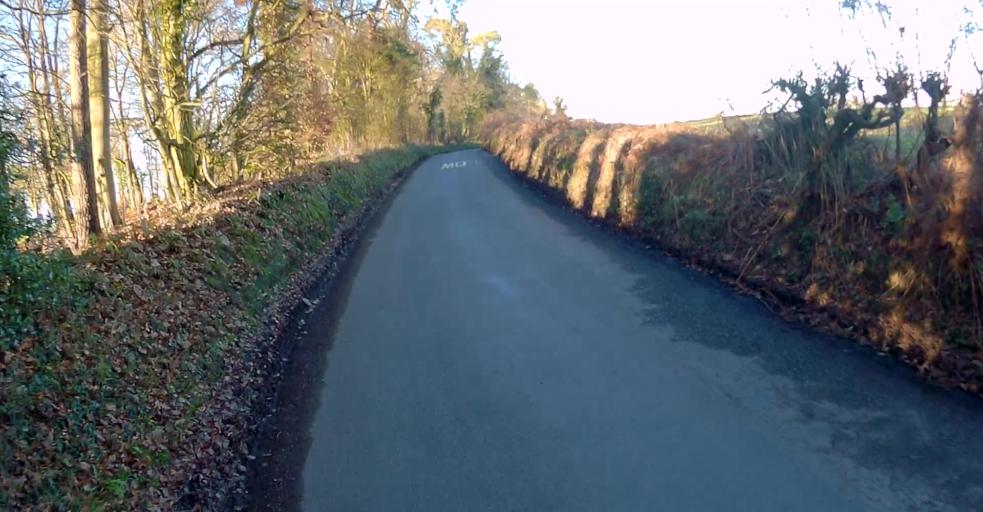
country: GB
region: England
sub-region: Hampshire
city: Hook
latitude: 51.2959
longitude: -0.9818
